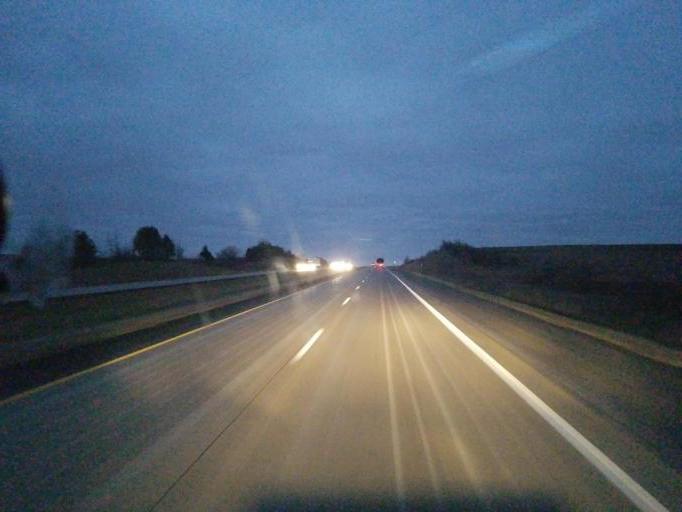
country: US
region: Iowa
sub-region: Cass County
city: Atlantic
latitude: 41.4971
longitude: -94.8250
